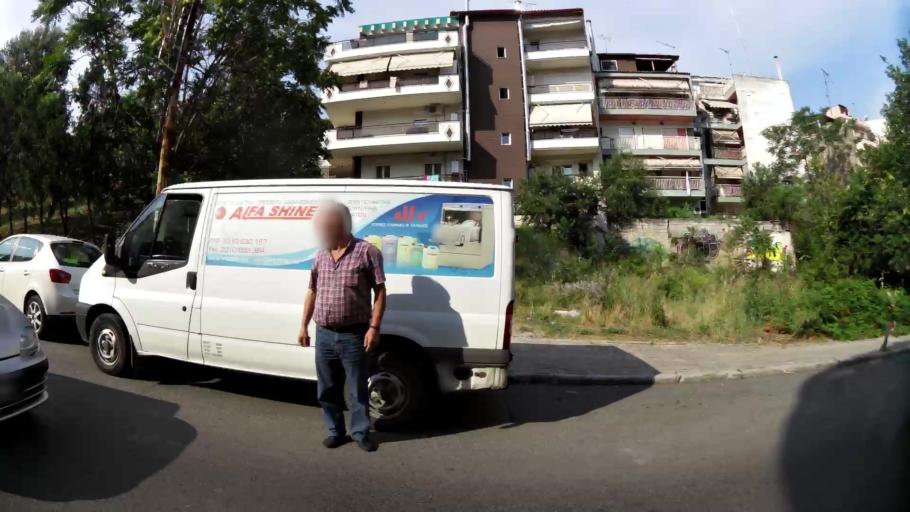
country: GR
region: Central Macedonia
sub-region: Nomos Thessalonikis
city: Sykies
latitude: 40.6456
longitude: 22.9528
